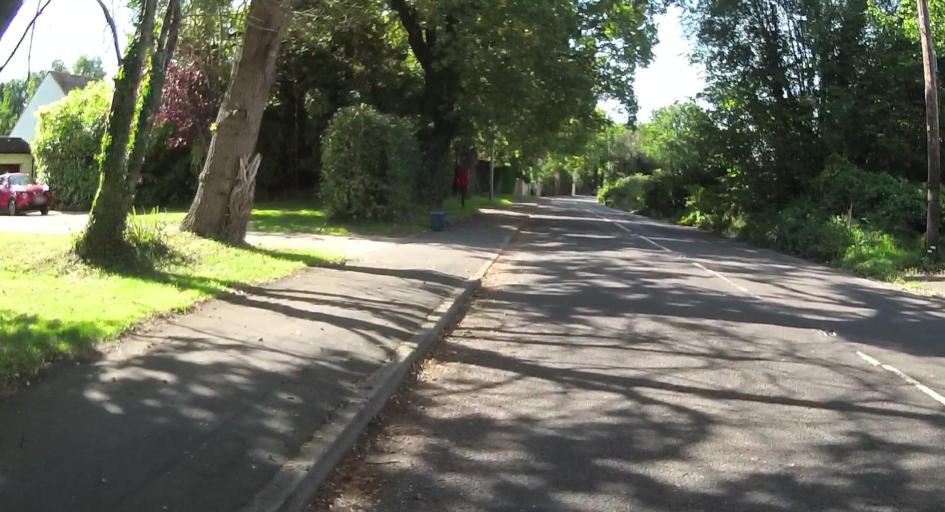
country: GB
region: England
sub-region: Surrey
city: Chertsey
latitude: 51.3890
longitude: -0.5316
